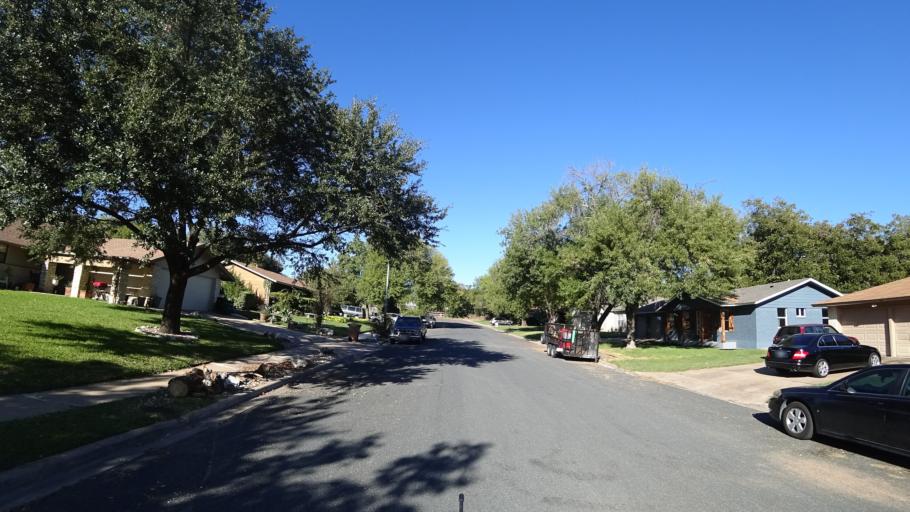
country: US
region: Texas
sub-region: Travis County
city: Austin
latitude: 30.2904
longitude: -97.6739
